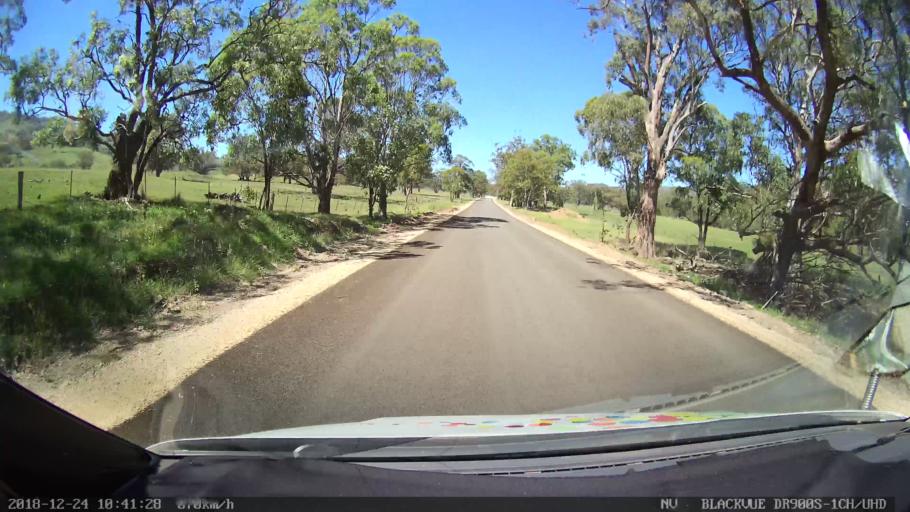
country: AU
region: New South Wales
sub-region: Upper Hunter Shire
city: Merriwa
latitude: -31.8691
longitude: 150.4590
